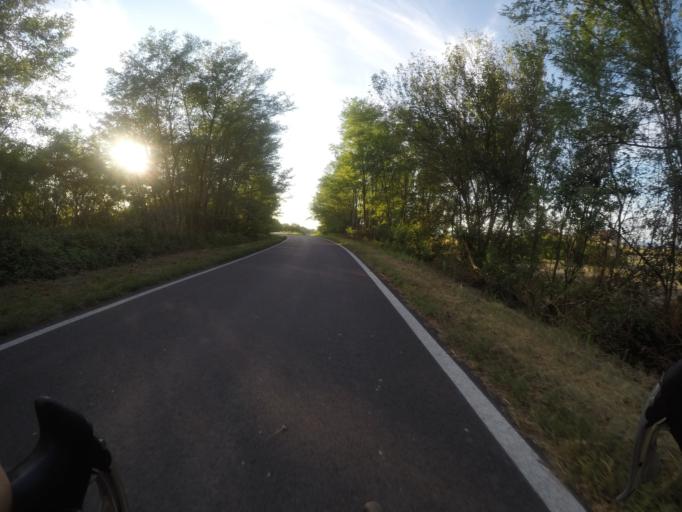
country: IT
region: Veneto
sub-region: Provincia di Rovigo
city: San Bellino
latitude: 44.9973
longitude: 11.5880
